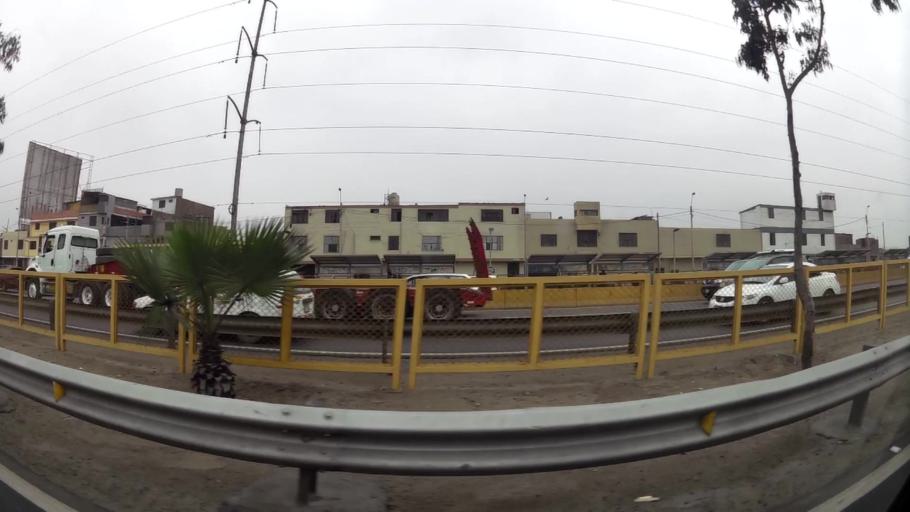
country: PE
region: Lima
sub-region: Lima
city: Surco
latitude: -12.1717
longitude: -76.9785
